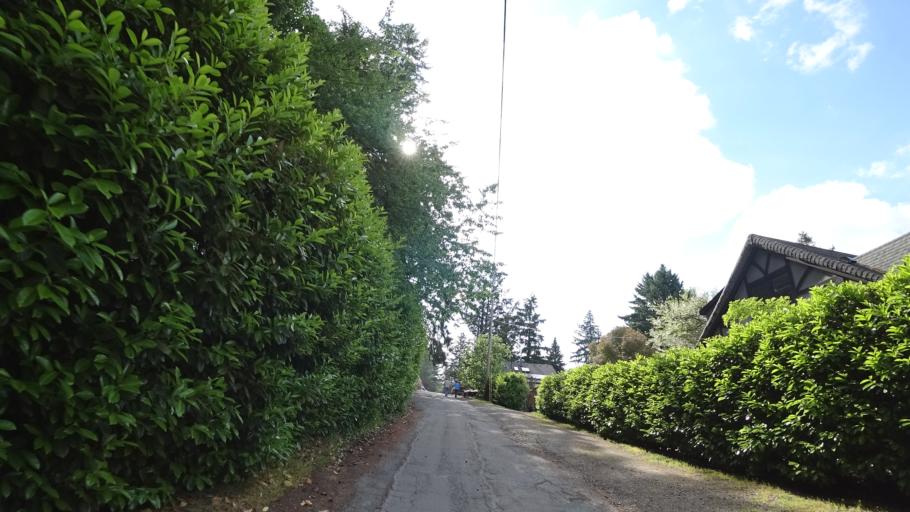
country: US
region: Oregon
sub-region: Washington County
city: Garden Home-Whitford
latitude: 45.4636
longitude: -122.7157
